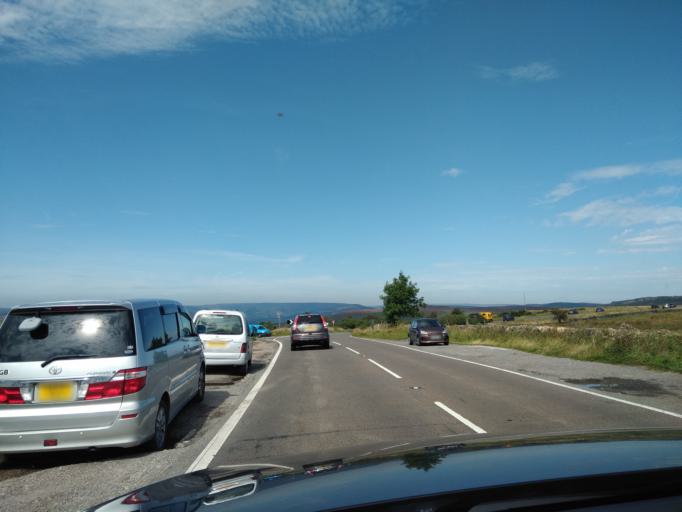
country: GB
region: England
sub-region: Derbyshire
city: Hathersage
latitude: 53.3064
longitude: -1.5974
